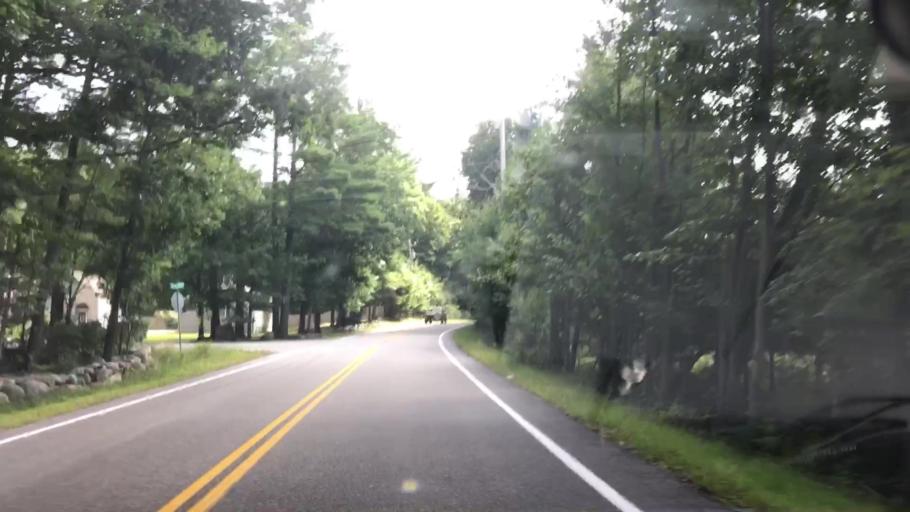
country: US
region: New Hampshire
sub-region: Hillsborough County
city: Bedford
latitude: 42.9189
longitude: -71.5690
